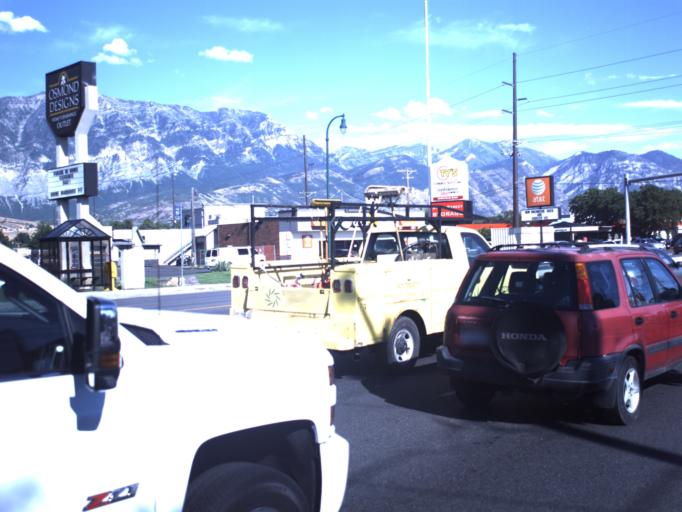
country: US
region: Utah
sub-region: Utah County
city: Lindon
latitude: 40.3273
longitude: -111.7084
